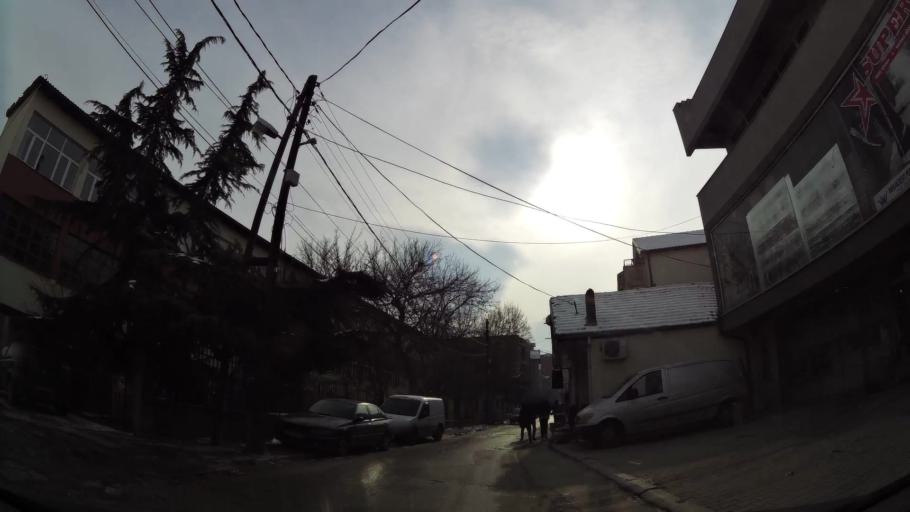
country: MK
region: Karpos
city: Skopje
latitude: 42.0055
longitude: 21.4359
